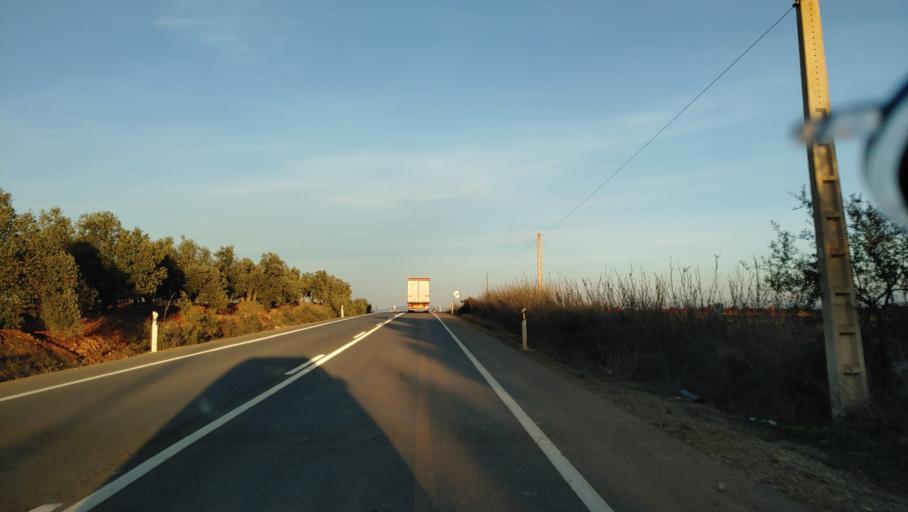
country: ES
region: Andalusia
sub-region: Provincia de Malaga
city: Humilladero
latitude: 37.0571
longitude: -4.7354
